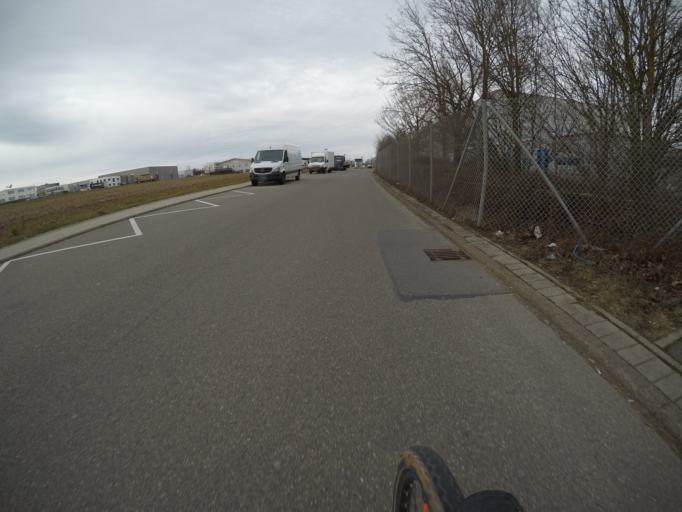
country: DE
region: Baden-Wuerttemberg
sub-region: Regierungsbezirk Stuttgart
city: Nufringen
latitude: 48.6297
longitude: 8.8983
